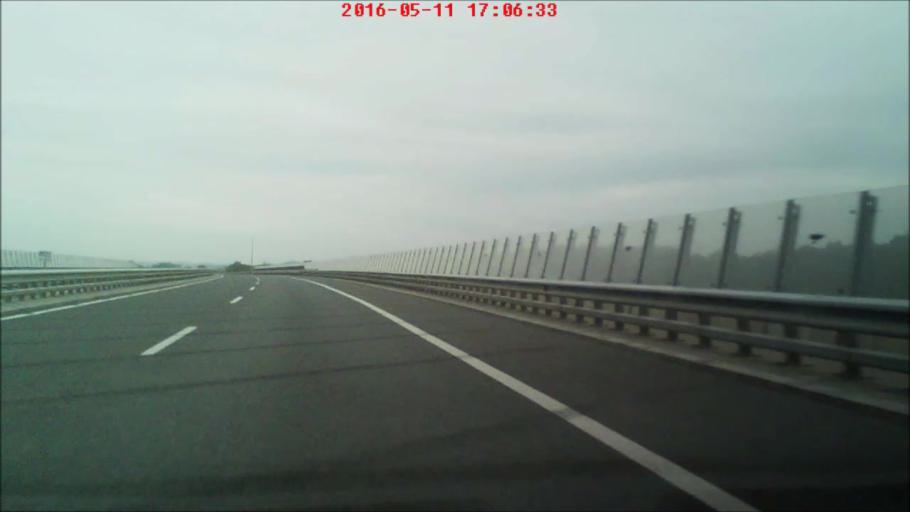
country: SI
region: Hajdina
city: Spodnja Hajdina
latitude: 46.4019
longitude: 15.8283
